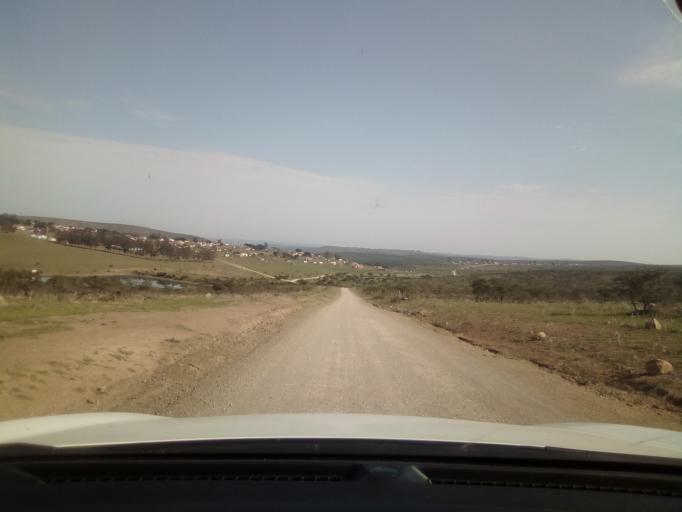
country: ZA
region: Eastern Cape
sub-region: Buffalo City Metropolitan Municipality
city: Bhisho
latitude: -32.9874
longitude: 27.2468
